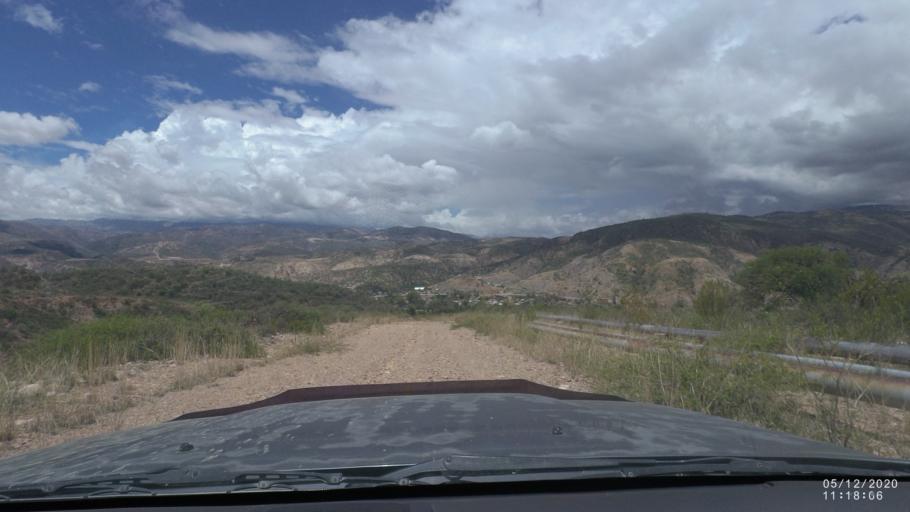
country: BO
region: Cochabamba
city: Sipe Sipe
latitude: -17.5524
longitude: -66.3323
